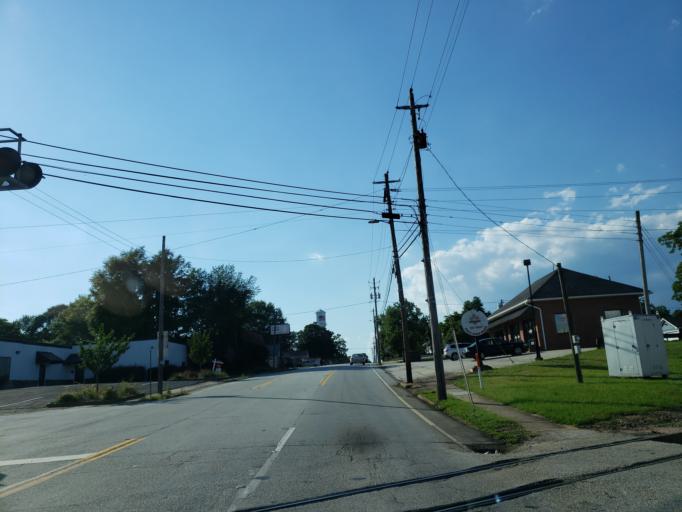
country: US
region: Georgia
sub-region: Haralson County
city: Bremen
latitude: 33.7221
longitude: -85.1465
